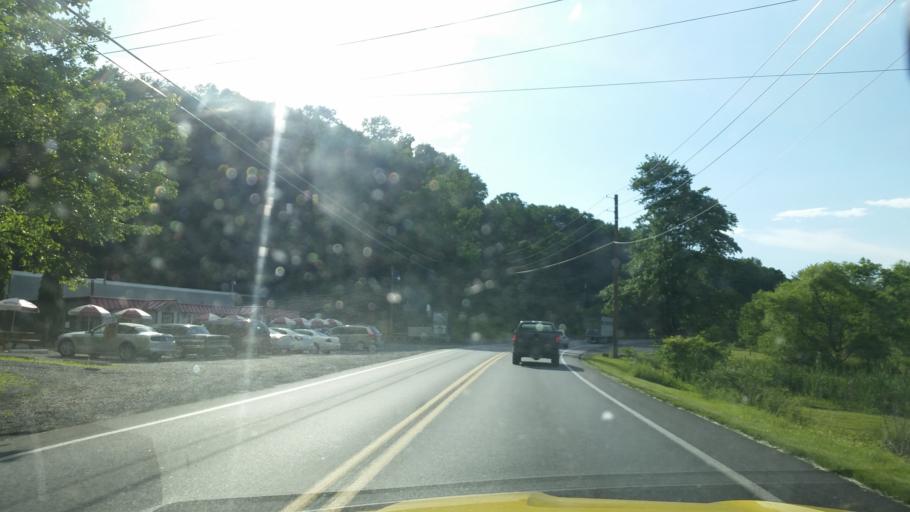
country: US
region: Pennsylvania
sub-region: Lancaster County
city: Brickerville
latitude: 40.2469
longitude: -76.3029
